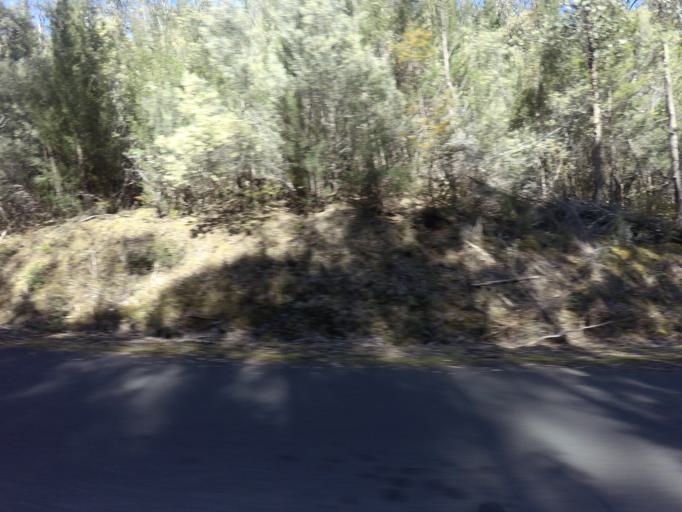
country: AU
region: Tasmania
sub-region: Derwent Valley
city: New Norfolk
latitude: -42.7236
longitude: 146.4354
